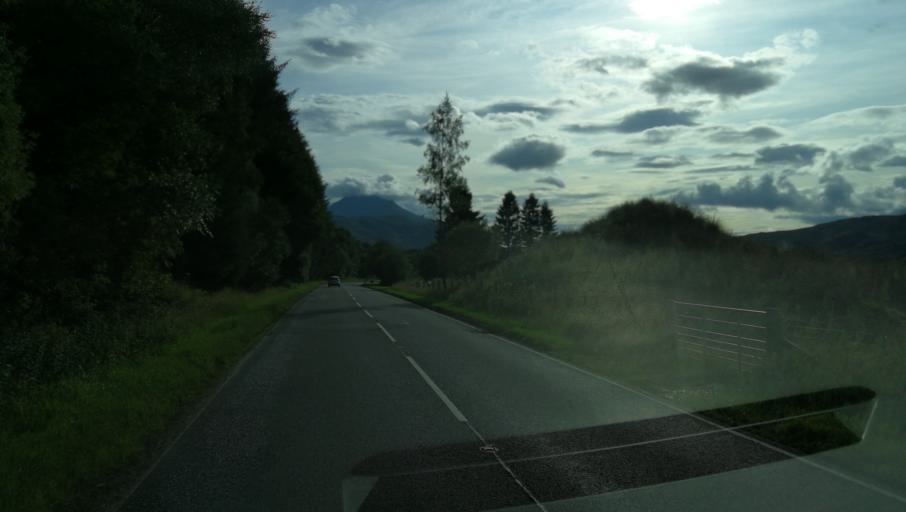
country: GB
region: Scotland
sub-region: Stirling
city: Callander
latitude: 56.4324
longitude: -4.3883
